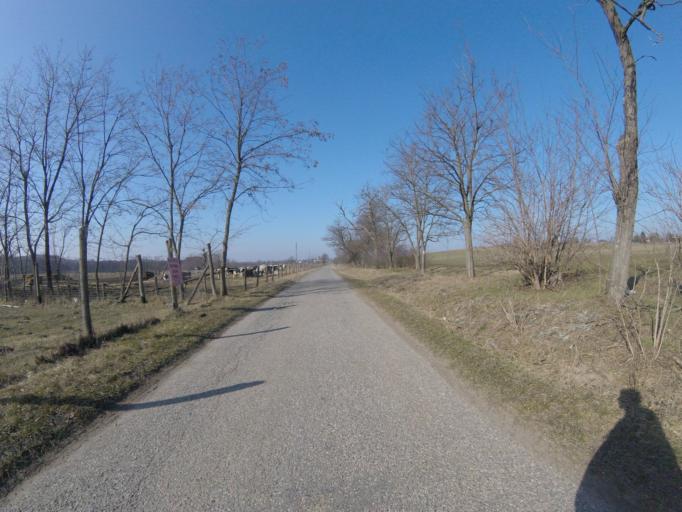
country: HU
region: Komarom-Esztergom
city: Oroszlany
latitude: 47.4712
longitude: 18.3357
